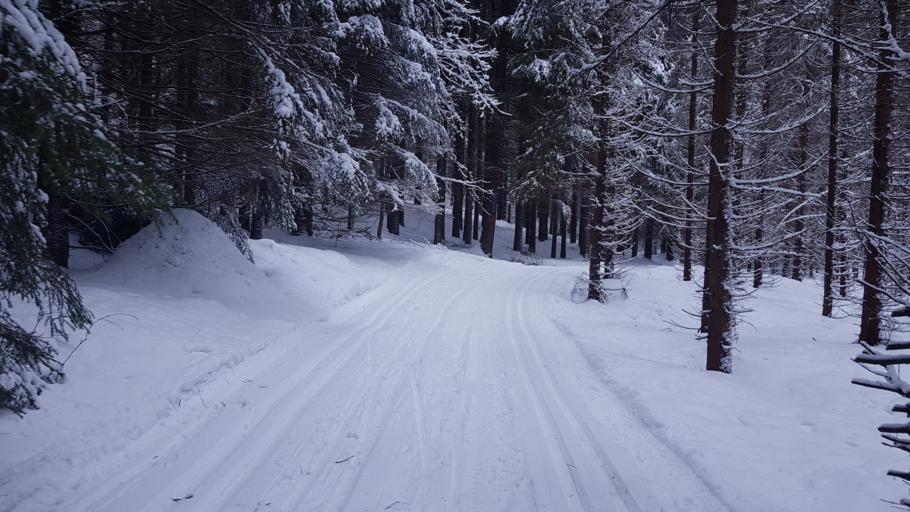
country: NO
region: Akershus
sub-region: Lorenskog
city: Kjenn
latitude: 59.9019
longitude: 10.8766
